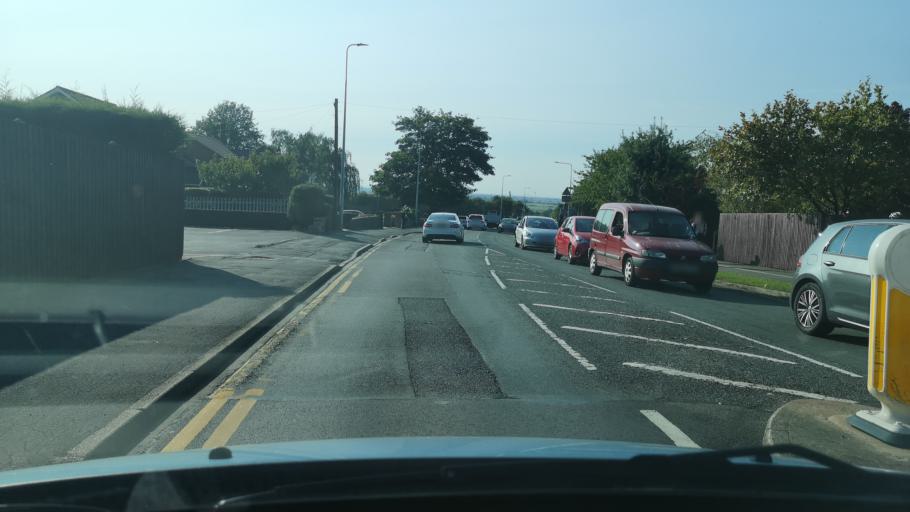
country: GB
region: England
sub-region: North Lincolnshire
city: Scunthorpe
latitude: 53.5738
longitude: -0.6651
